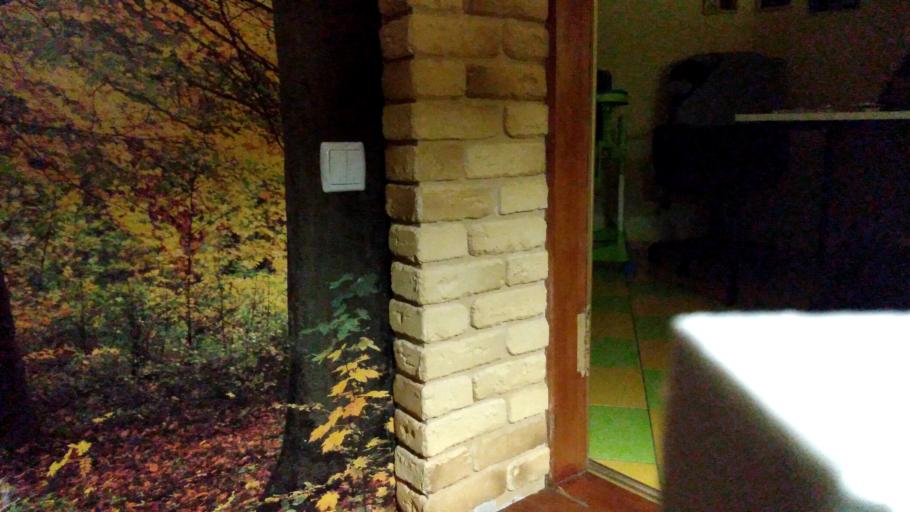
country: RU
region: Vologda
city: Lipin Bor
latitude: 60.9193
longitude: 37.9900
